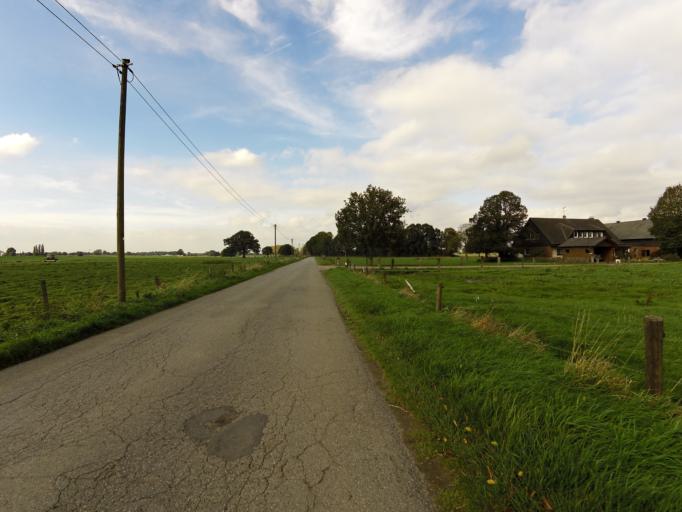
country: DE
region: North Rhine-Westphalia
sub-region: Regierungsbezirk Dusseldorf
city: Hamminkeln
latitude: 51.7858
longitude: 6.5556
